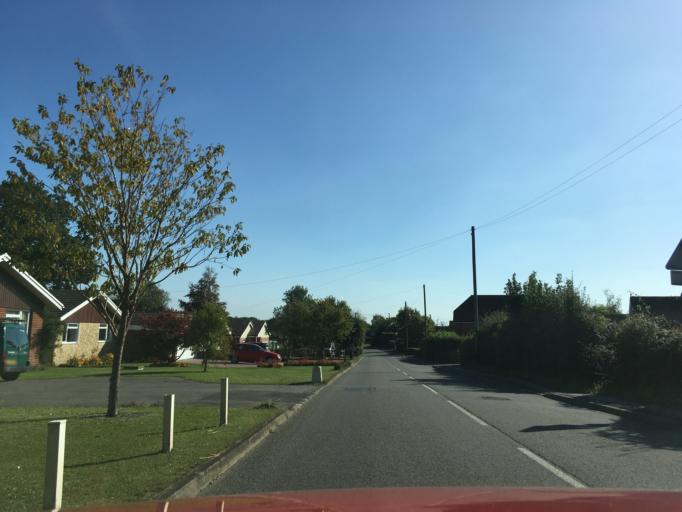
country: GB
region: England
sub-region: West Berkshire
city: Cold Ash
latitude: 51.4198
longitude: -1.2637
